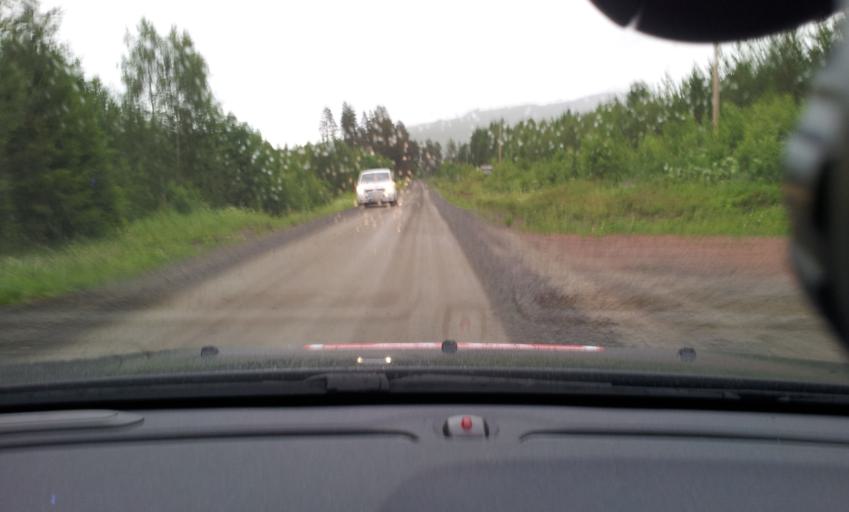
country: SE
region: Jaemtland
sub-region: Ragunda Kommun
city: Hammarstrand
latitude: 63.1372
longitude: 16.2443
